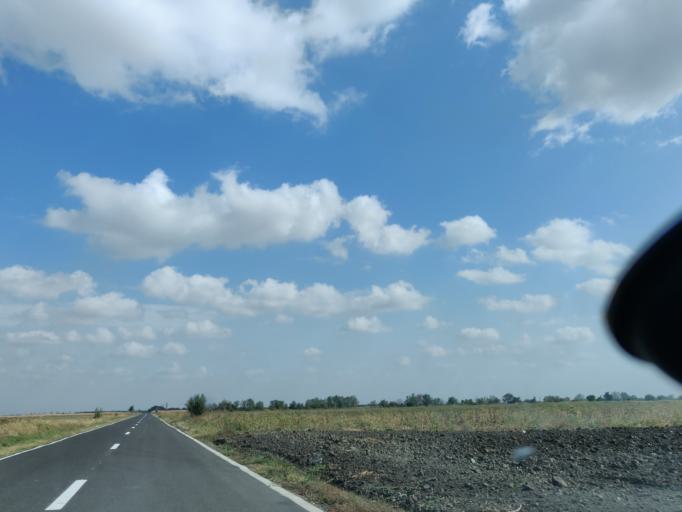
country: RO
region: Vrancea
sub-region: Comuna Maicanesti
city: Ramniceni
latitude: 45.4678
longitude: 27.4232
